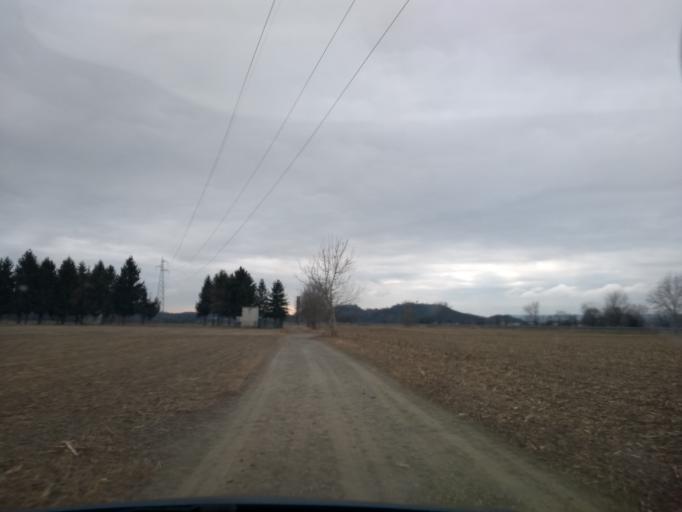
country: IT
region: Piedmont
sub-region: Provincia di Torino
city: Fiorano Canavese
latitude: 45.4762
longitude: 7.8421
